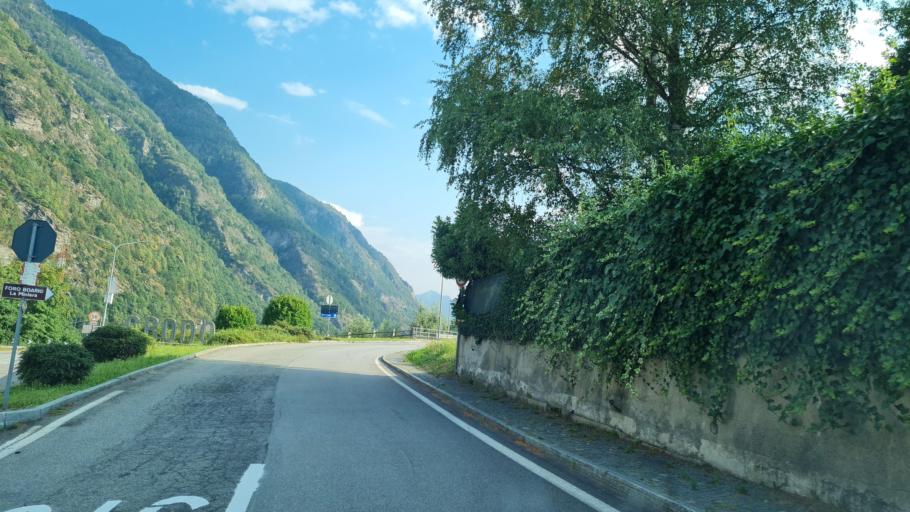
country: IT
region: Piedmont
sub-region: Provincia Verbano-Cusio-Ossola
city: Crodo
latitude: 46.2271
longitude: 8.3253
